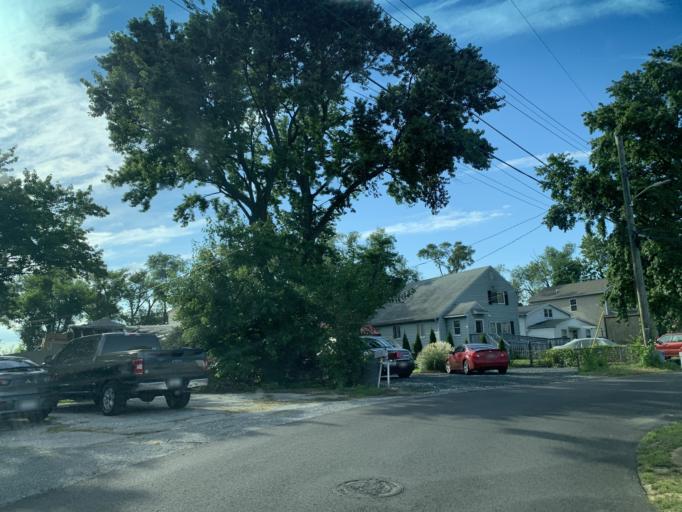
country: US
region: Maryland
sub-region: Baltimore County
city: Essex
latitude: 39.3048
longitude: -76.4892
